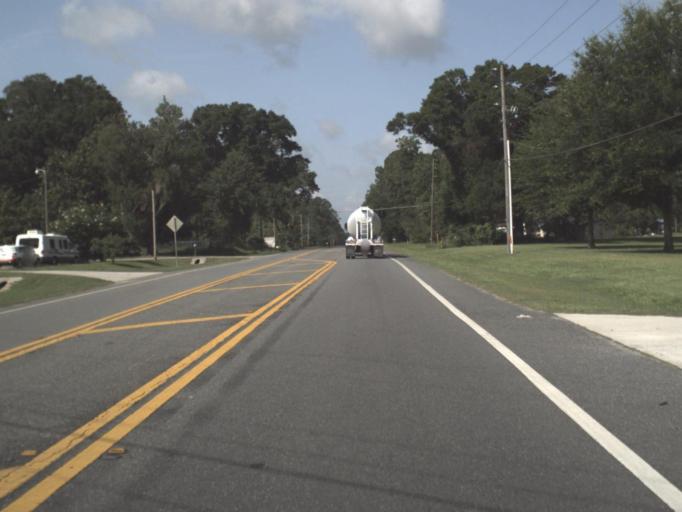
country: US
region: Florida
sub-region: Columbia County
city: Lake City
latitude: 30.1446
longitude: -82.7016
